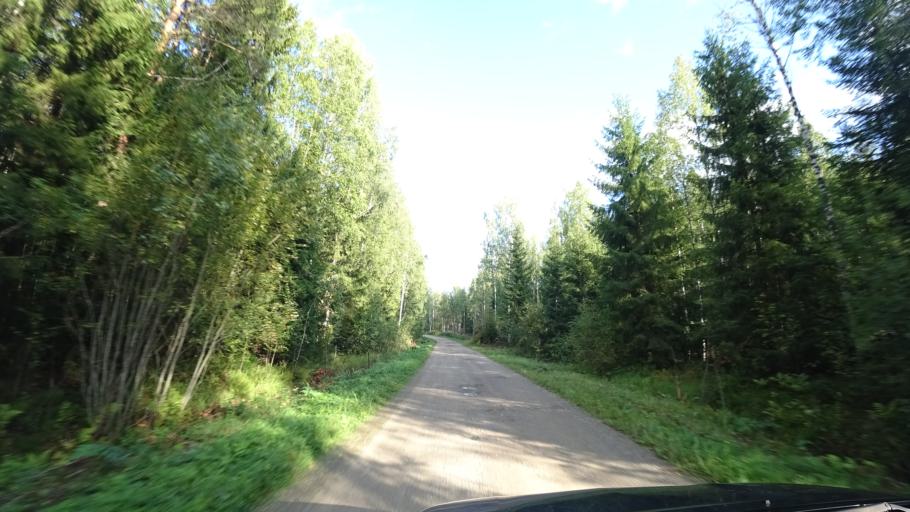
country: FI
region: Paijanne Tavastia
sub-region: Lahti
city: Auttoinen
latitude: 61.2127
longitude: 25.1617
